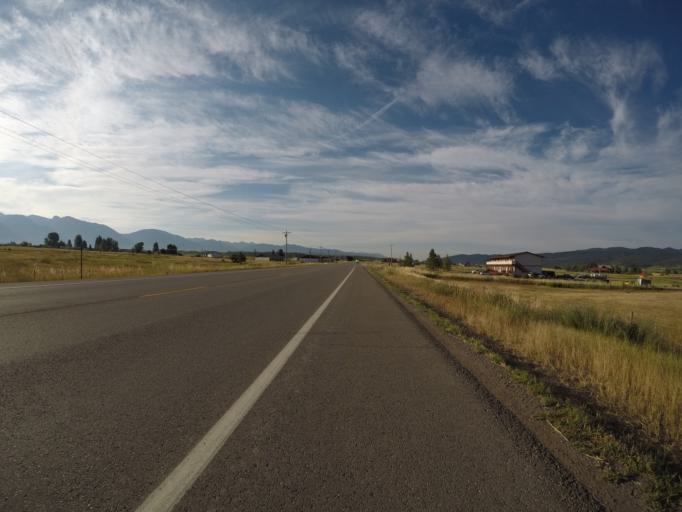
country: US
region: Wyoming
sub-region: Lincoln County
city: Afton
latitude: 42.9478
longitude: -111.0096
